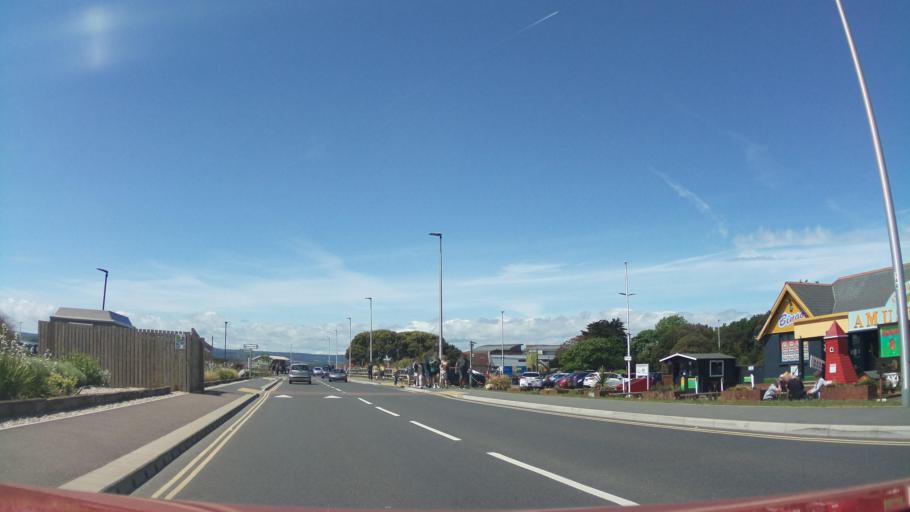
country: GB
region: England
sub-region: Devon
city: Exmouth
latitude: 50.6126
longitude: -3.4072
